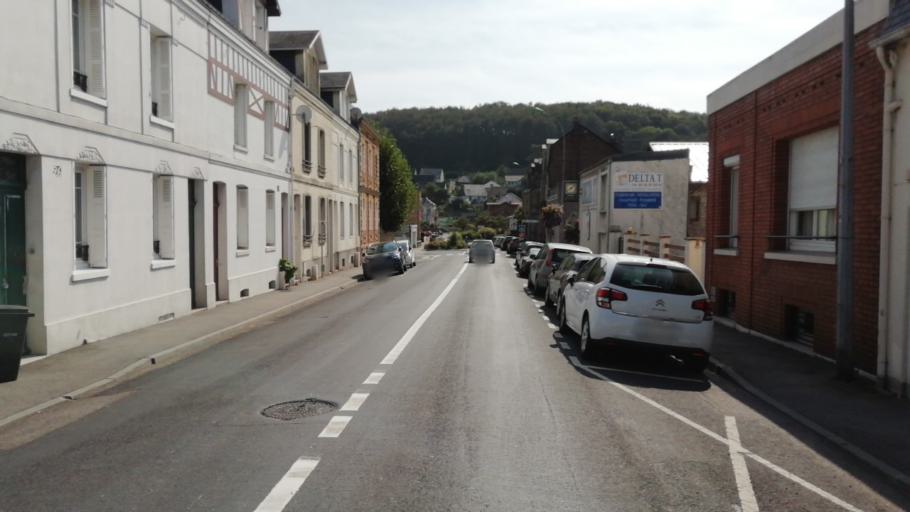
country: FR
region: Haute-Normandie
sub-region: Departement de la Seine-Maritime
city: Montivilliers
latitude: 49.5447
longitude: 0.1887
